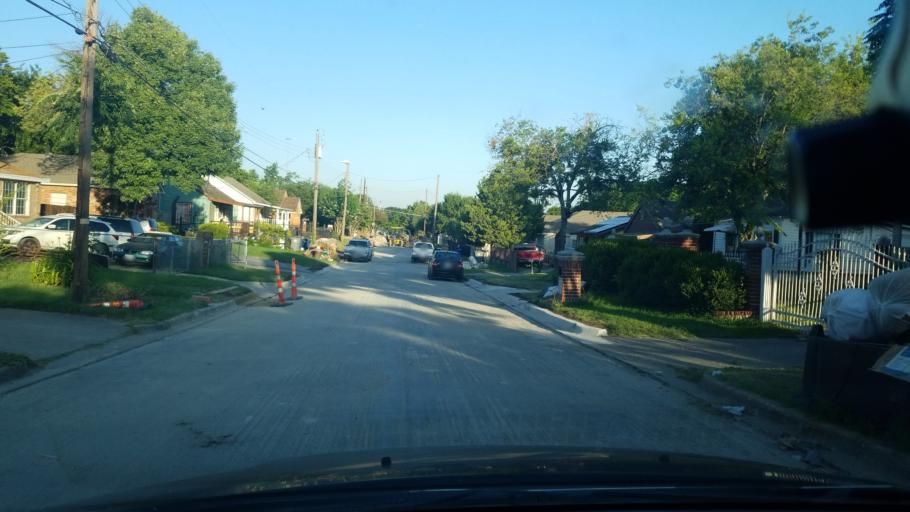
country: US
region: Texas
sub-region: Dallas County
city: Cockrell Hill
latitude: 32.7176
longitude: -96.8250
